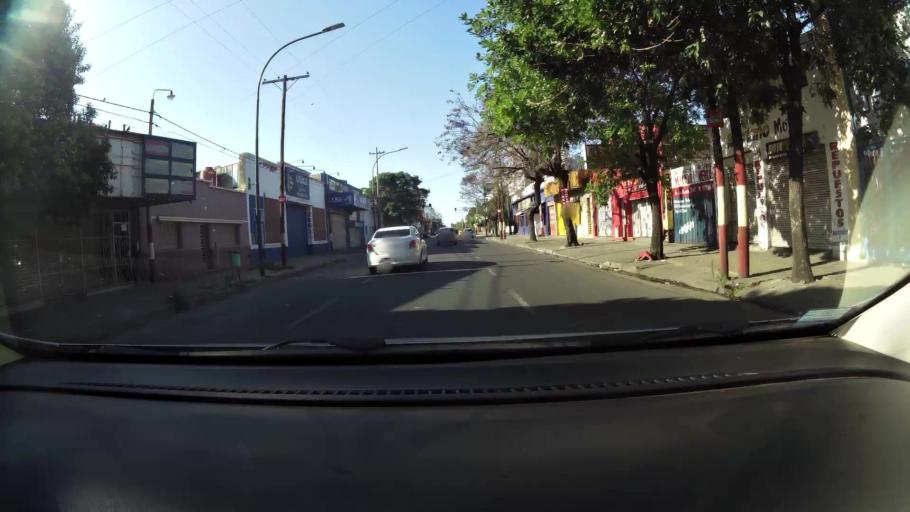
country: AR
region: Cordoba
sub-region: Departamento de Capital
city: Cordoba
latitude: -31.3863
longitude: -64.1760
